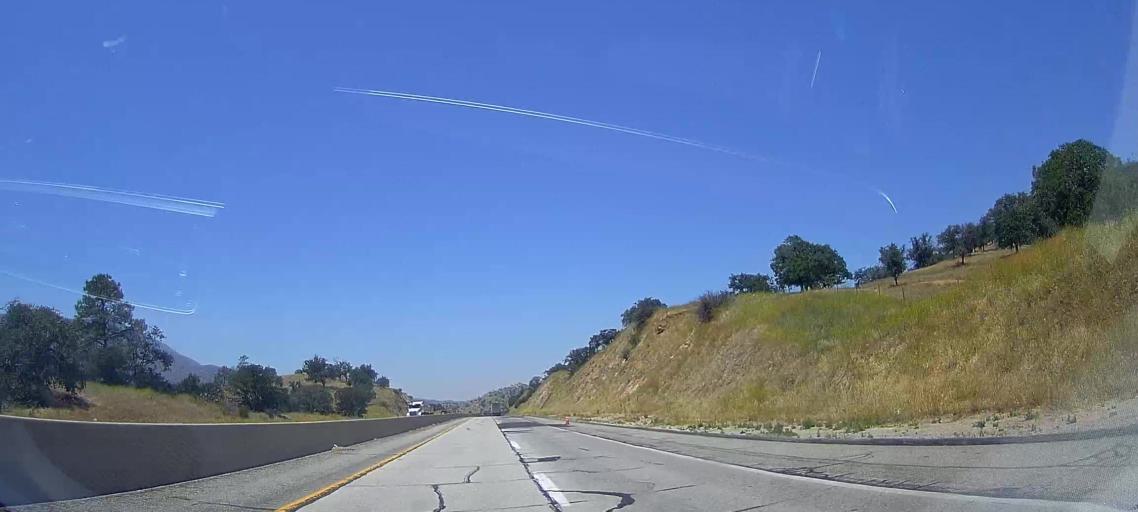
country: US
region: California
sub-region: Kern County
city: Golden Hills
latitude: 35.1930
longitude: -118.5108
